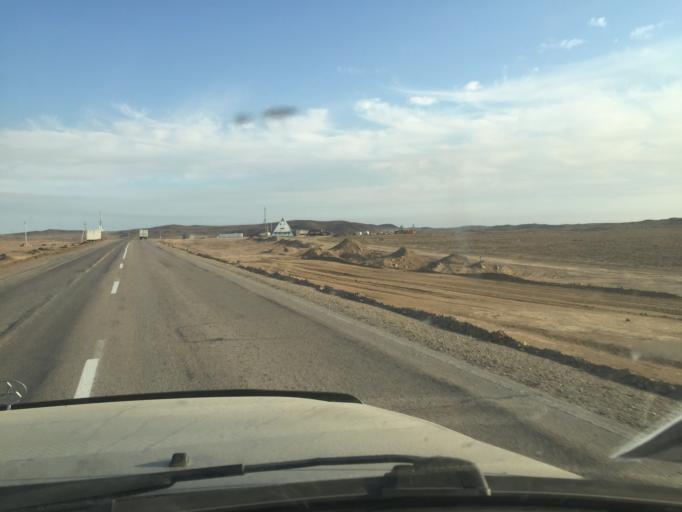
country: KZ
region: Zhambyl
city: Mynaral
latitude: 45.4529
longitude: 73.5981
